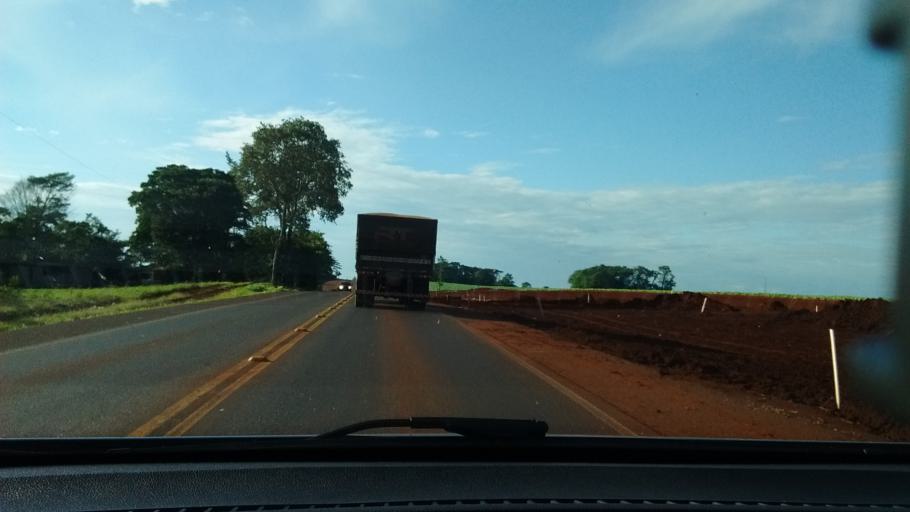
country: BR
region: Parana
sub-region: Cascavel
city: Cascavel
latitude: -25.1734
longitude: -53.6035
